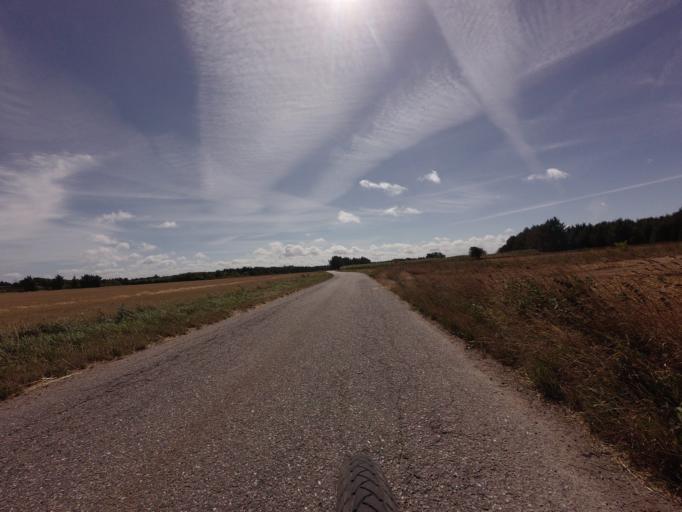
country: DK
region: North Denmark
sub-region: Hjorring Kommune
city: Vra
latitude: 57.3822
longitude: 9.7835
